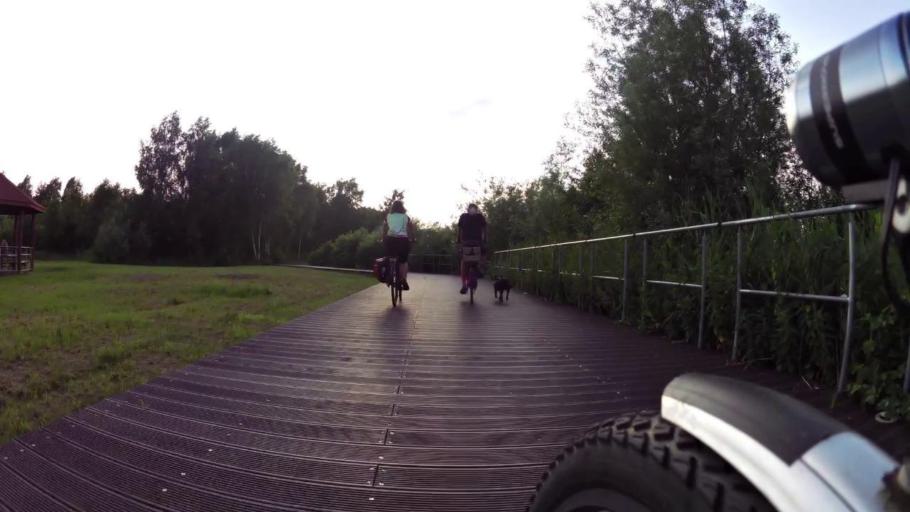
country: PL
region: West Pomeranian Voivodeship
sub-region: Powiat goleniowski
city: Stepnica
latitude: 53.6666
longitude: 14.5054
